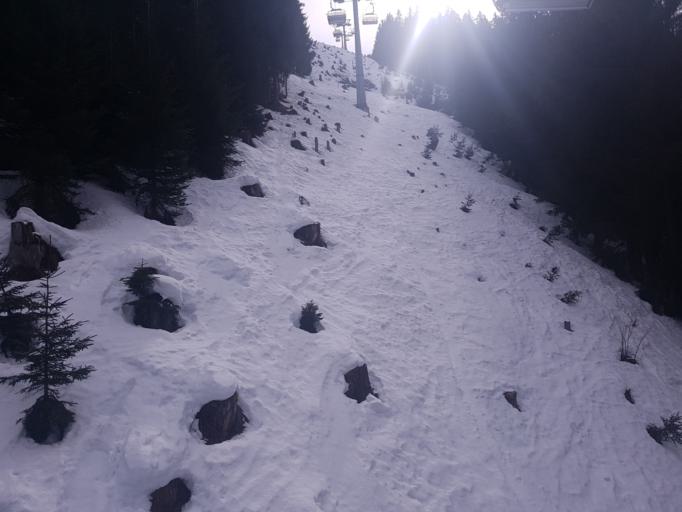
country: AT
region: Tyrol
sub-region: Politischer Bezirk Kufstein
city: Worgl
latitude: 47.4402
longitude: 12.0853
